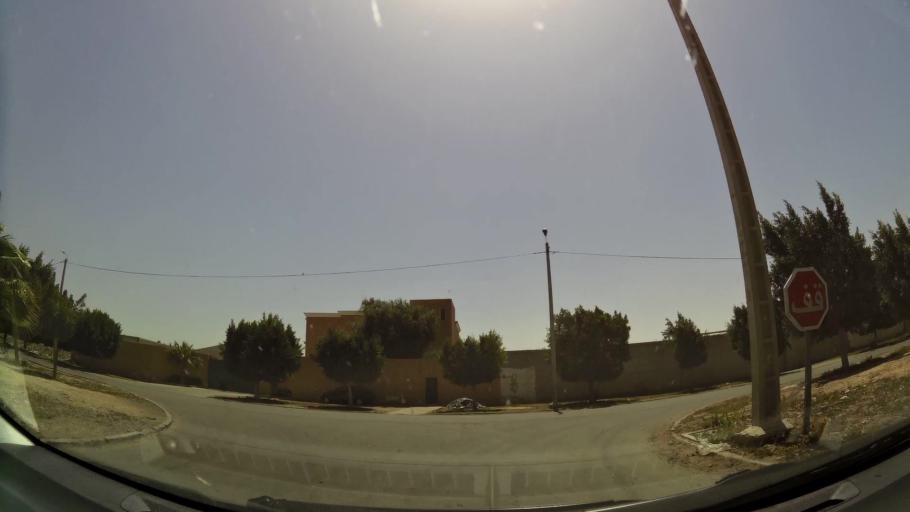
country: MA
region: Souss-Massa-Draa
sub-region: Inezgane-Ait Mellou
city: Inezgane
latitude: 30.3385
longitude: -9.4859
